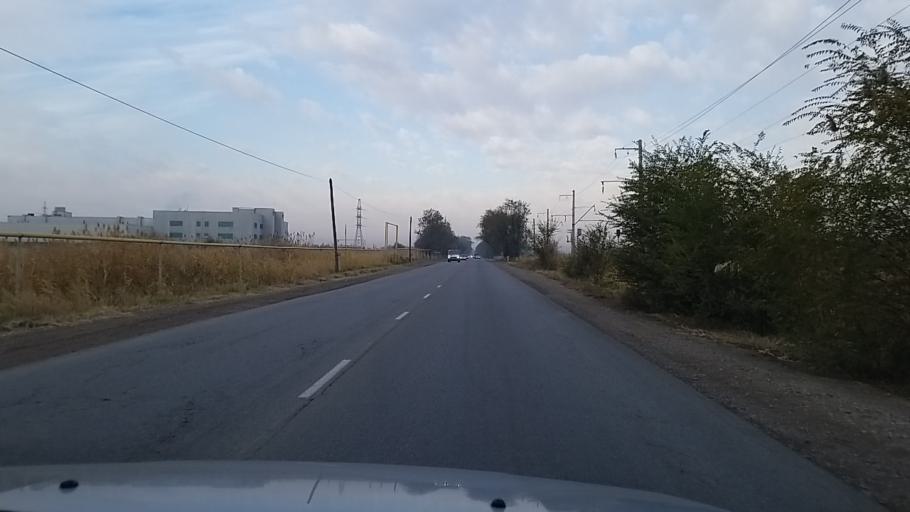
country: KZ
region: Almaty Oblysy
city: Burunday
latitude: 43.3575
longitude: 76.7854
